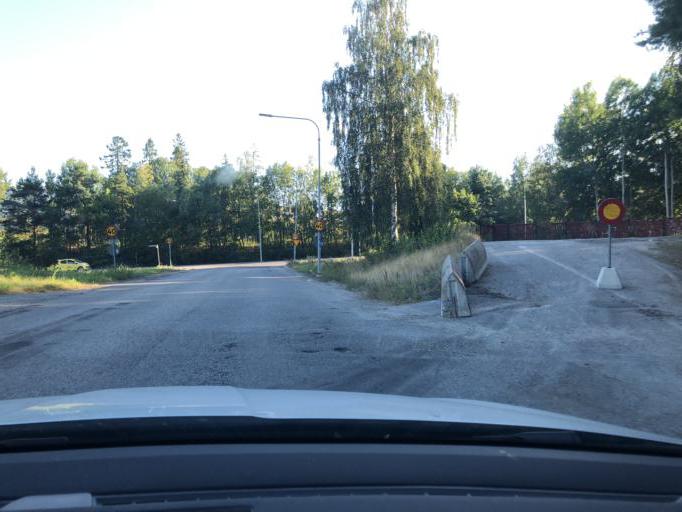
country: SE
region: Stockholm
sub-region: Sodertalje Kommun
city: Soedertaelje
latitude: 59.1782
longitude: 17.6205
